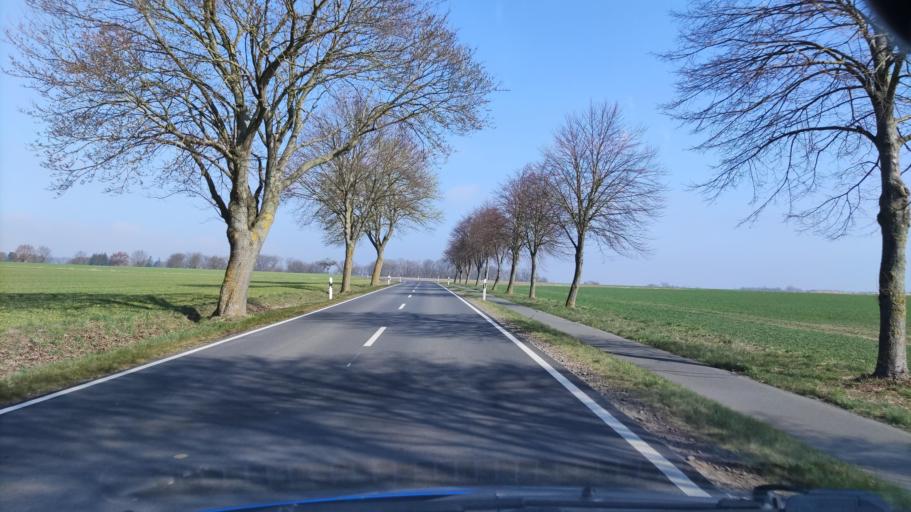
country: DE
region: Lower Saxony
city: Clenze
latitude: 52.9585
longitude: 10.9726
